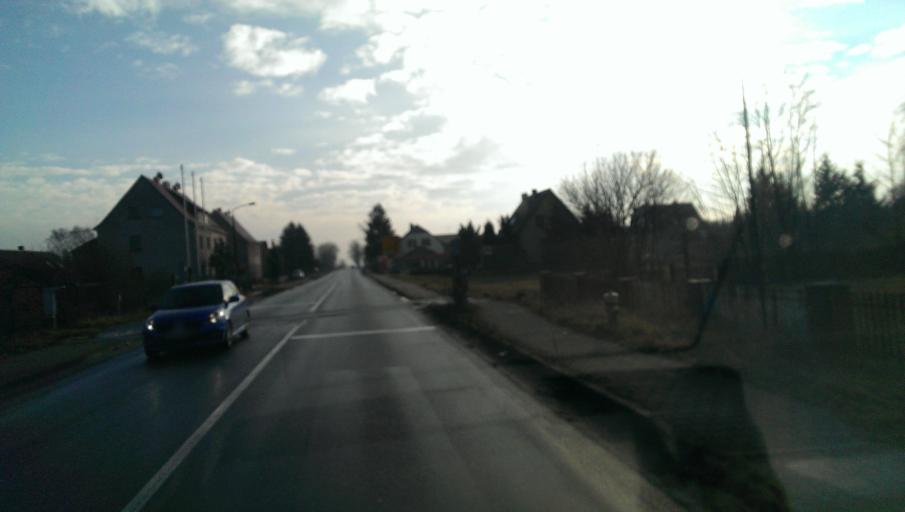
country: DE
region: Brandenburg
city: Herzberg
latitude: 51.6943
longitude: 13.2504
